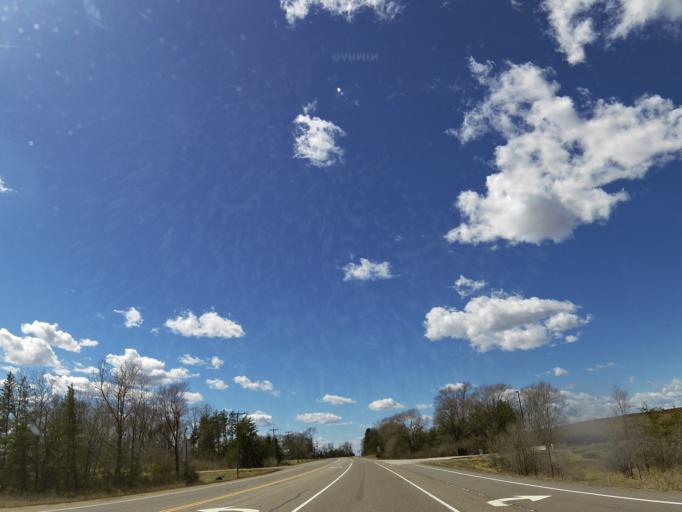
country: US
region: Minnesota
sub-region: Dakota County
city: Rosemount
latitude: 44.7178
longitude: -93.0862
